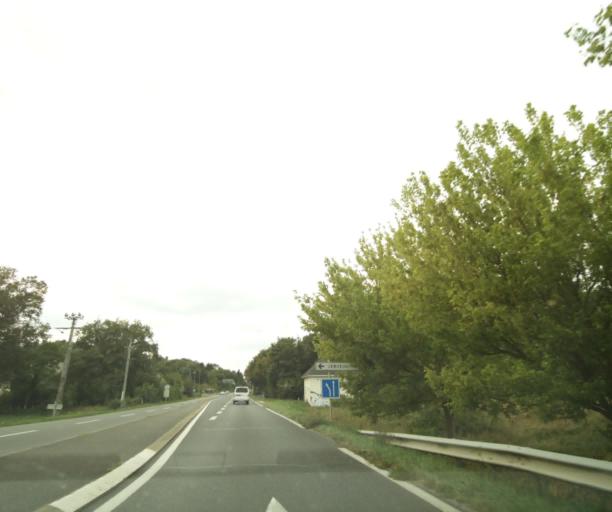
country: FR
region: Centre
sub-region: Departement d'Indre-et-Loire
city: Perrusson
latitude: 47.0761
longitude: 1.0599
